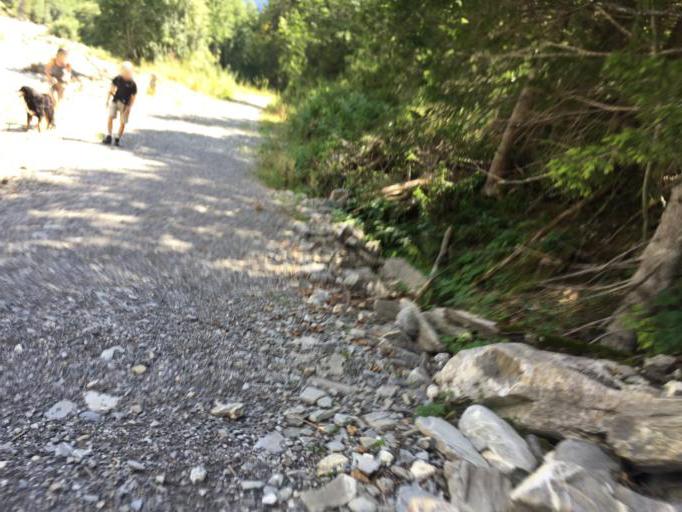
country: CH
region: Bern
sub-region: Frutigen-Niedersimmental District
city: Adelboden
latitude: 46.4851
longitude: 7.5299
